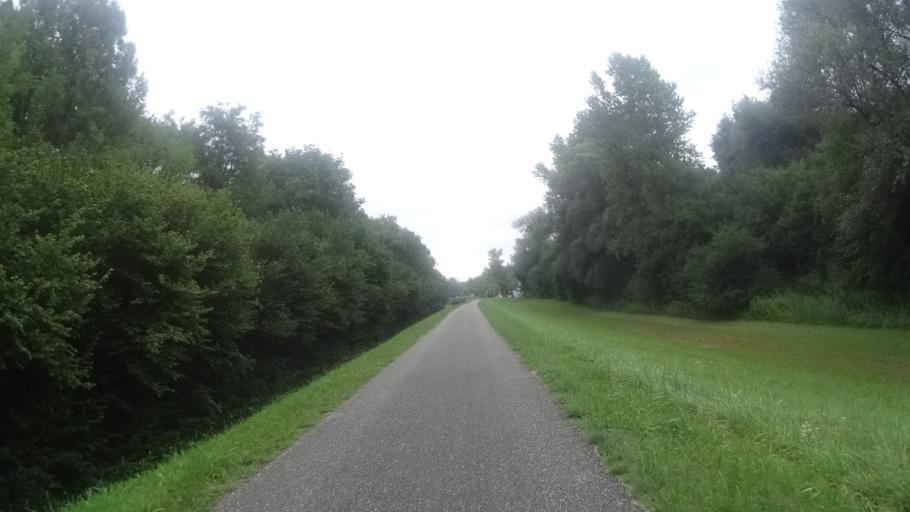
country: FR
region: Alsace
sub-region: Departement du Bas-Rhin
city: Seltz
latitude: 48.8870
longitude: 8.1304
